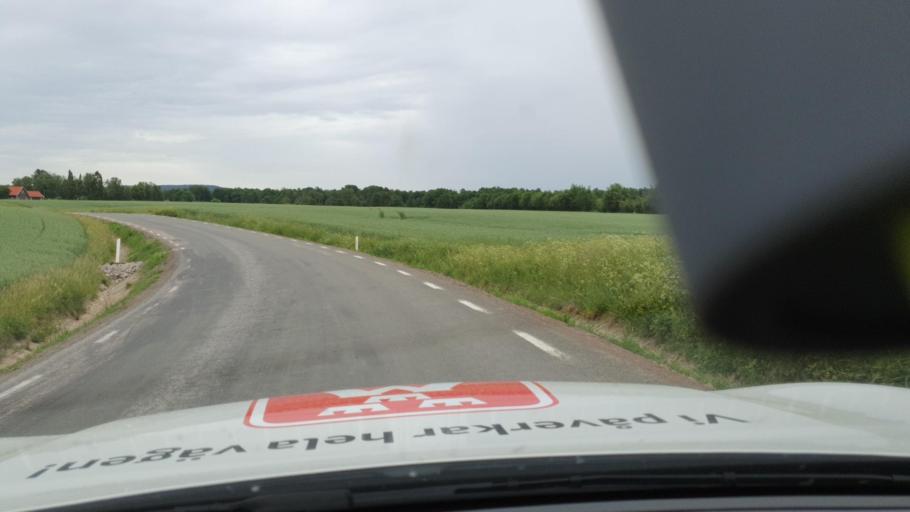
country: SE
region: Vaestra Goetaland
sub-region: Tidaholms Kommun
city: Olofstorp
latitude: 58.3037
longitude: 14.0644
